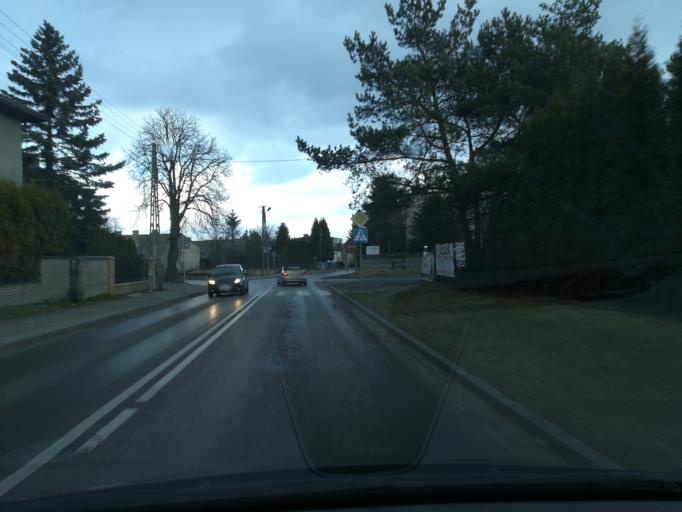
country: PL
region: Lodz Voivodeship
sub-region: Powiat radomszczanski
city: Radomsko
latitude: 51.0614
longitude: 19.4270
